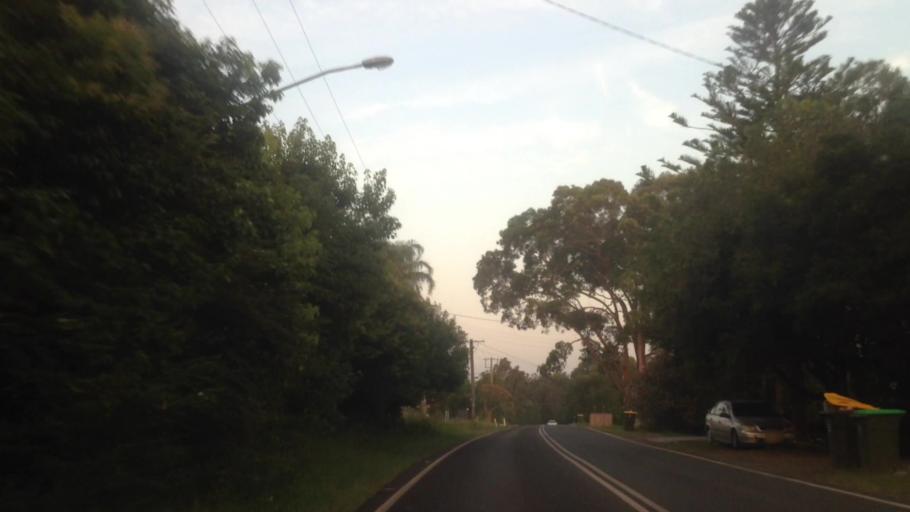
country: AU
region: New South Wales
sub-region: Lake Macquarie Shire
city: Dora Creek
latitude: -33.0799
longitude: 151.4942
